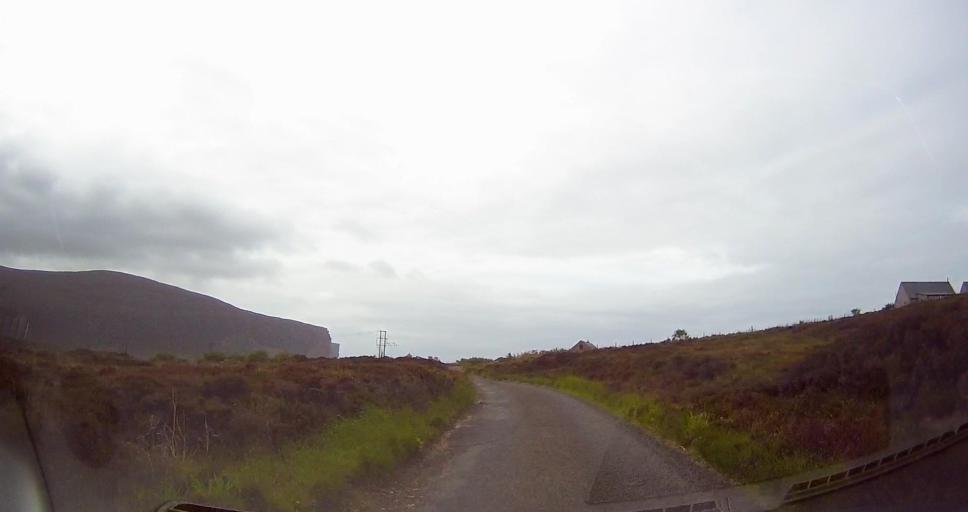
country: GB
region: Scotland
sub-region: Orkney Islands
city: Stromness
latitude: 58.8781
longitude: -3.3860
